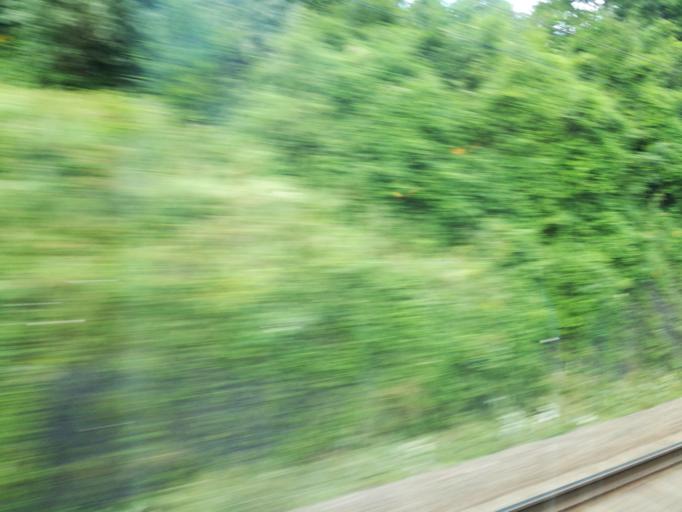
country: RO
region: Prahova
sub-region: Oras Sinaia
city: Sinaia
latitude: 45.3368
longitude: 25.5539
